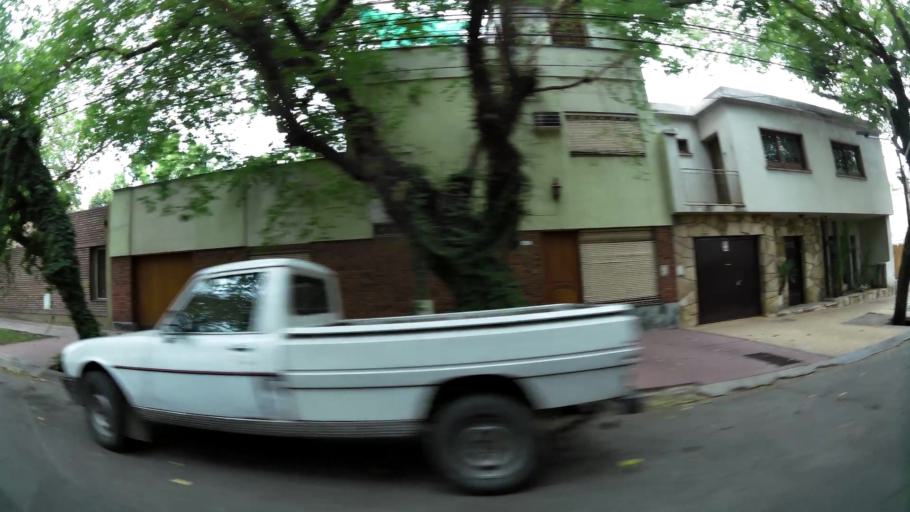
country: AR
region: Mendoza
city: Mendoza
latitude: -32.8893
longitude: -68.8402
